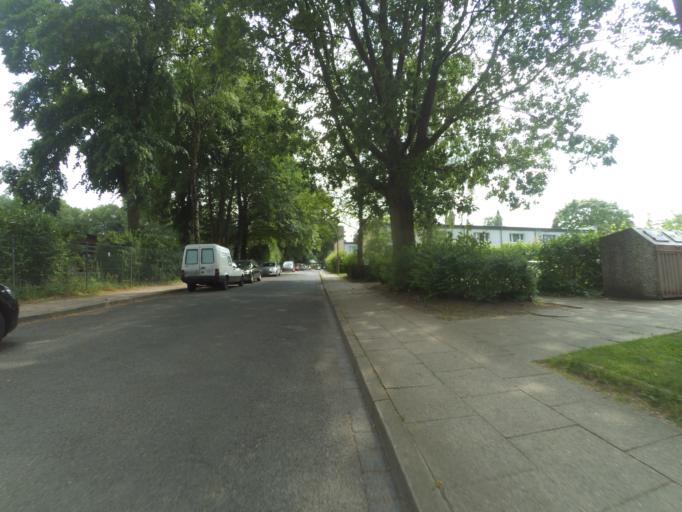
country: DE
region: Hamburg
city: Eidelstedt
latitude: 53.5789
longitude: 9.8703
